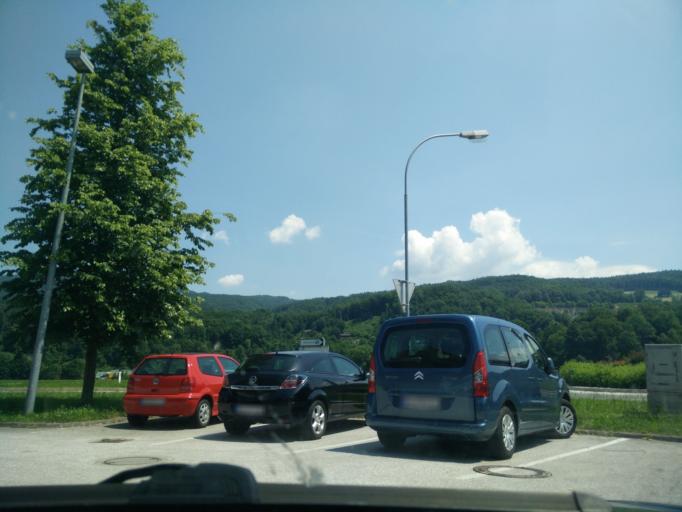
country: AT
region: Salzburg
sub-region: Politischer Bezirk Hallein
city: Puch bei Hallein
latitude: 47.7228
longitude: 13.0893
